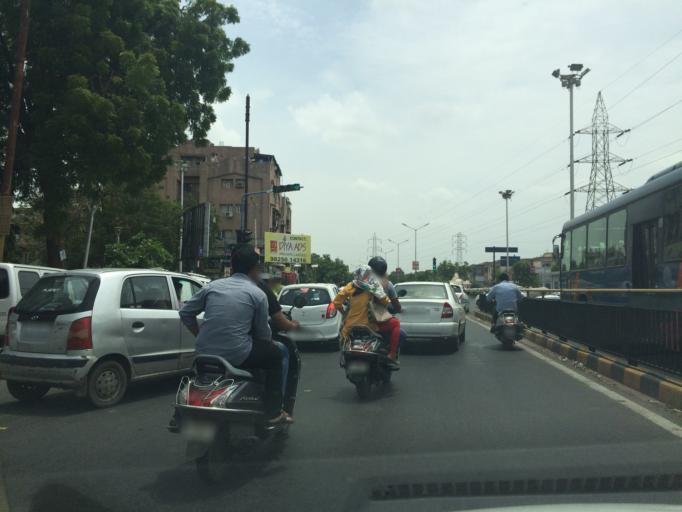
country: IN
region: Gujarat
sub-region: Ahmadabad
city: Ahmedabad
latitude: 23.0621
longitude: 72.5530
